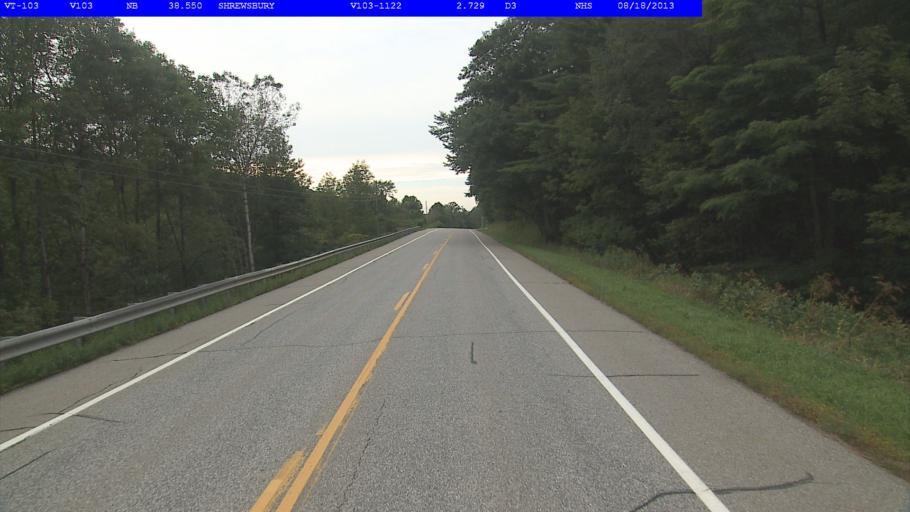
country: US
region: Vermont
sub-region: Rutland County
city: Rutland
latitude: 43.5095
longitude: -72.9091
